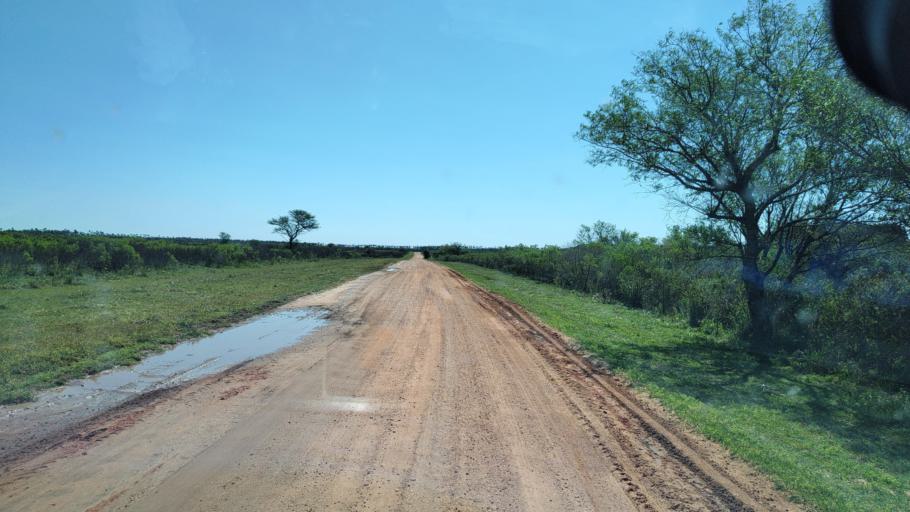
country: AR
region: Entre Rios
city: Ubajay
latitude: -31.8645
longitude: -58.2614
